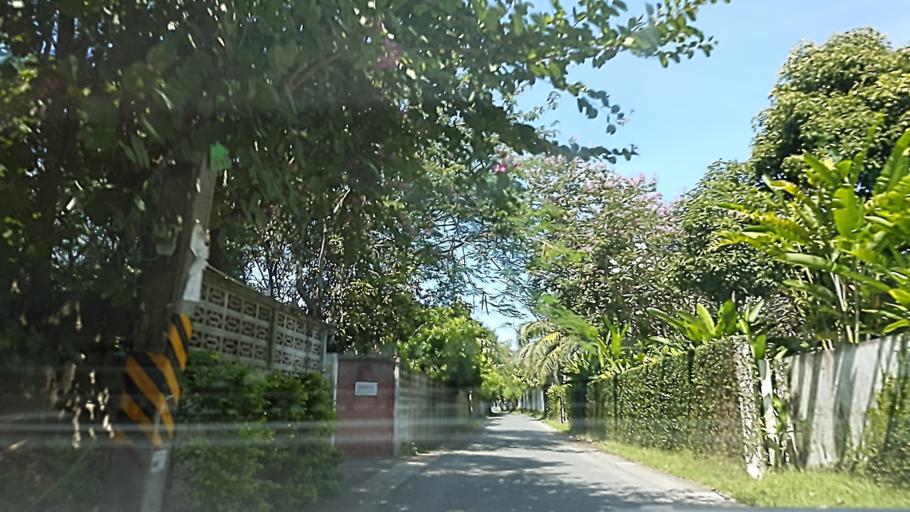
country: TH
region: Chiang Mai
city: Chiang Mai
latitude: 18.8236
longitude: 98.9563
